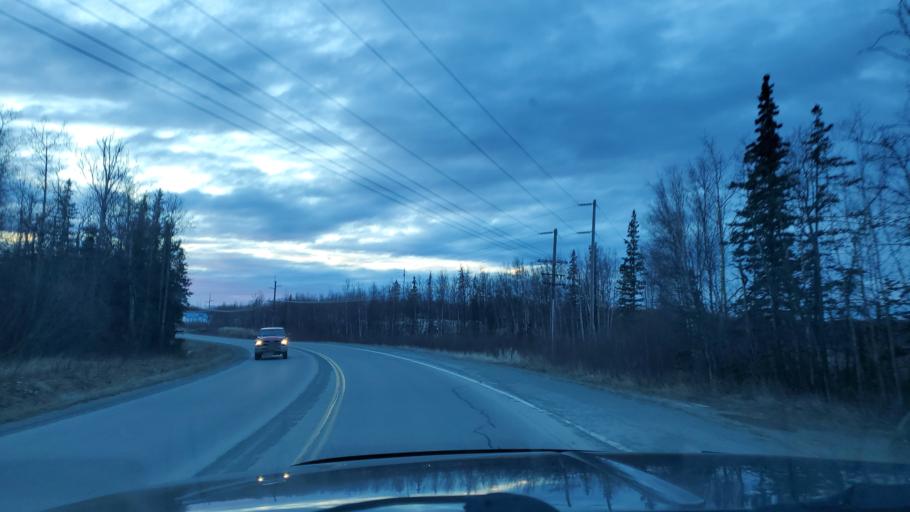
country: US
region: Alaska
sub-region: Matanuska-Susitna Borough
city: Lakes
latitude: 61.6050
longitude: -149.3501
